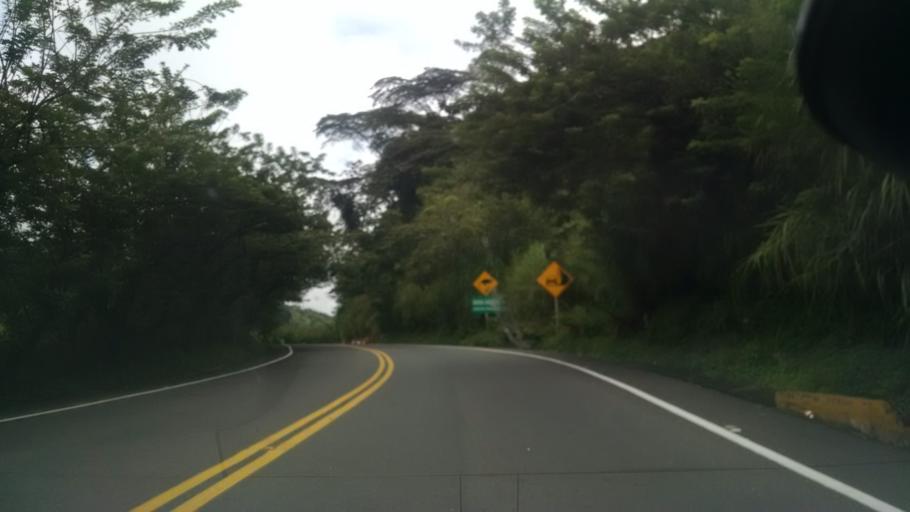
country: CO
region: Caldas
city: Palestina
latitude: 5.0515
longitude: -75.6029
